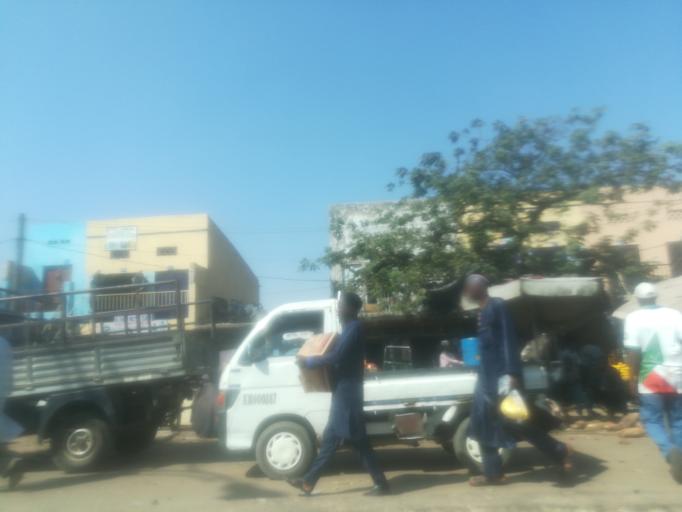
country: NG
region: Kano
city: Kano
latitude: 12.0130
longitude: 8.5346
